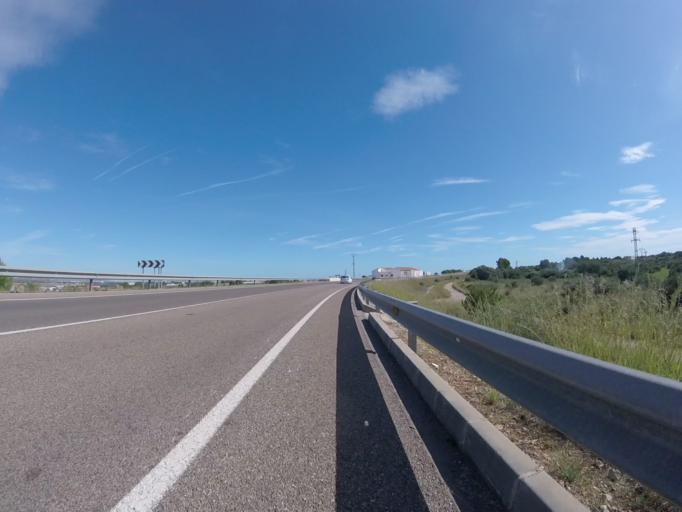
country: ES
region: Valencia
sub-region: Provincia de Castello
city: Peniscola
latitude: 40.3960
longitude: 0.3636
